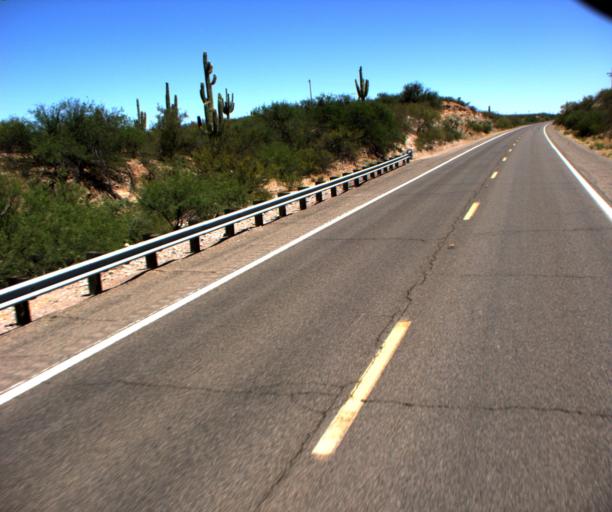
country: US
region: Arizona
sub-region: Pinal County
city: Mammoth
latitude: 32.8144
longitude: -110.6883
